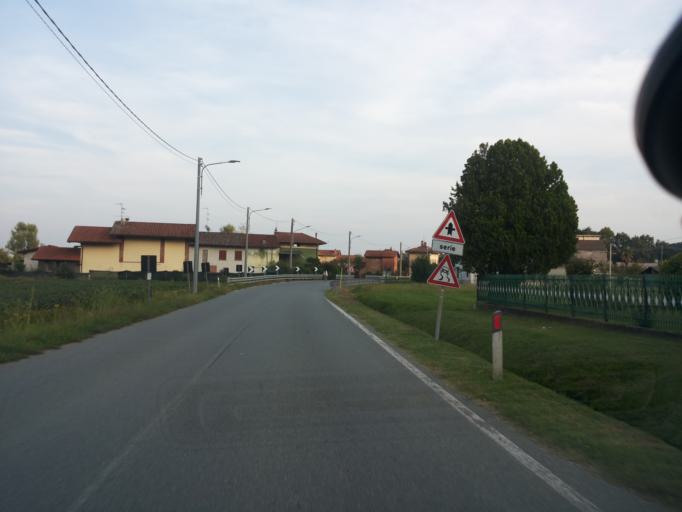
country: IT
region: Piedmont
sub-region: Provincia di Biella
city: Mottalciata
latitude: 45.5233
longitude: 8.1975
